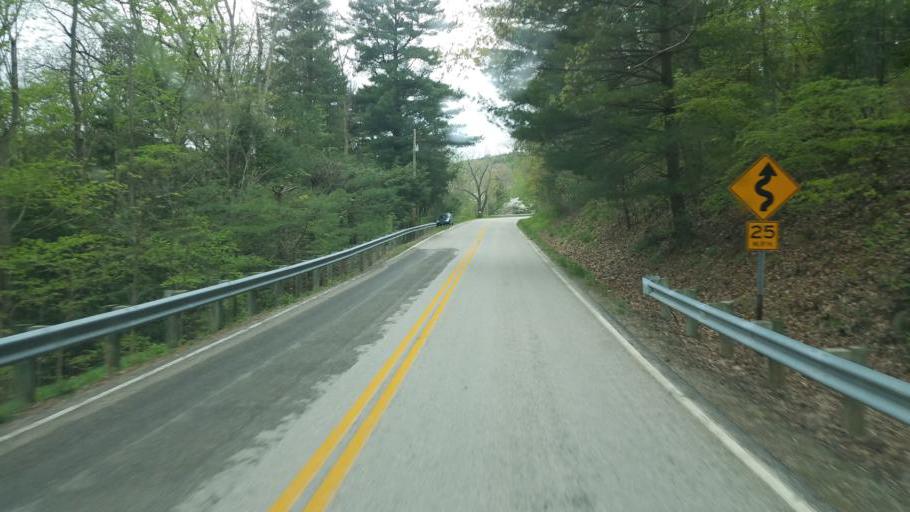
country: US
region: Ohio
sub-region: Ashland County
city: Loudonville
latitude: 40.6253
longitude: -82.3185
